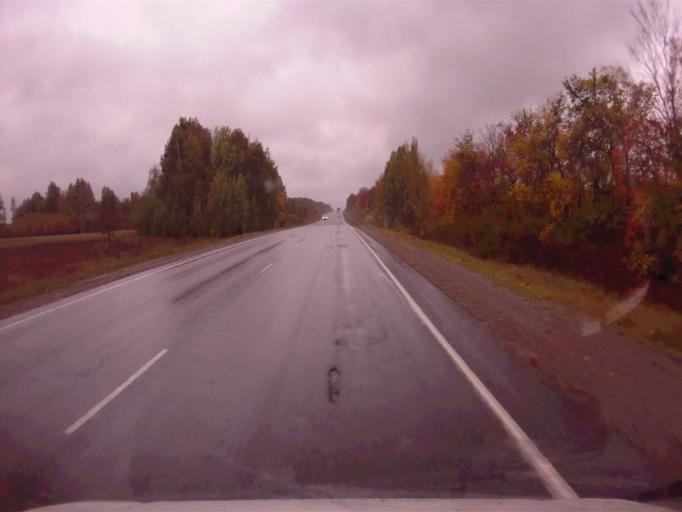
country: RU
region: Chelyabinsk
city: Novogornyy
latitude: 55.4888
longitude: 60.6971
